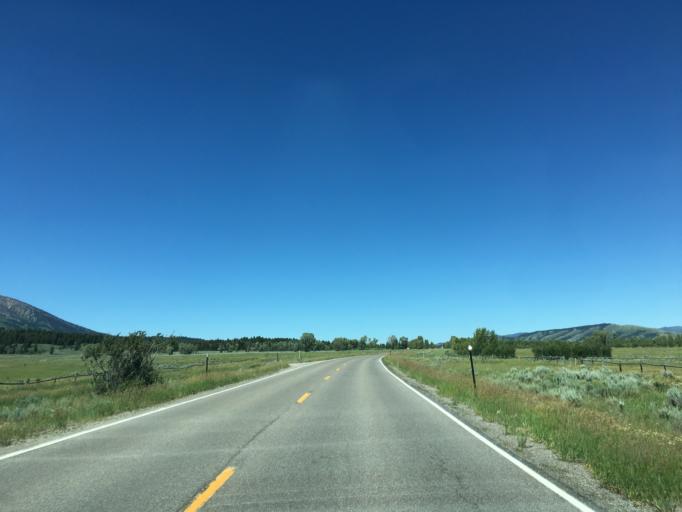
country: US
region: Wyoming
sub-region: Teton County
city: Moose Wilson Road
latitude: 43.5910
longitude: -110.8137
